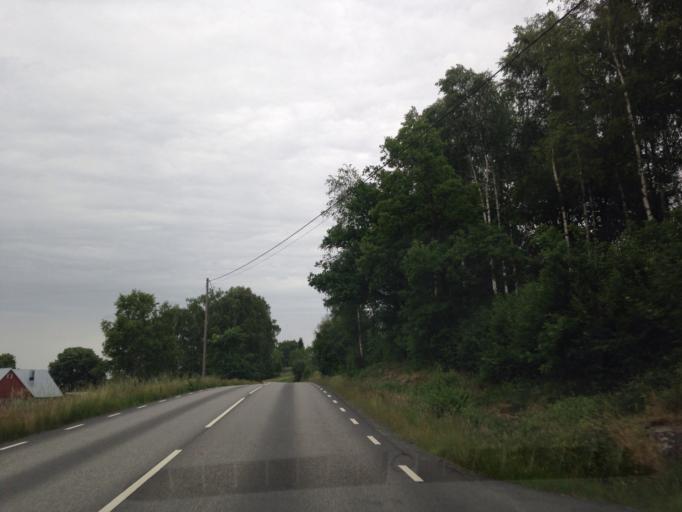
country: SE
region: Vaestra Goetaland
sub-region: Marks Kommun
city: Horred
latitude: 57.4826
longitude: 12.5205
